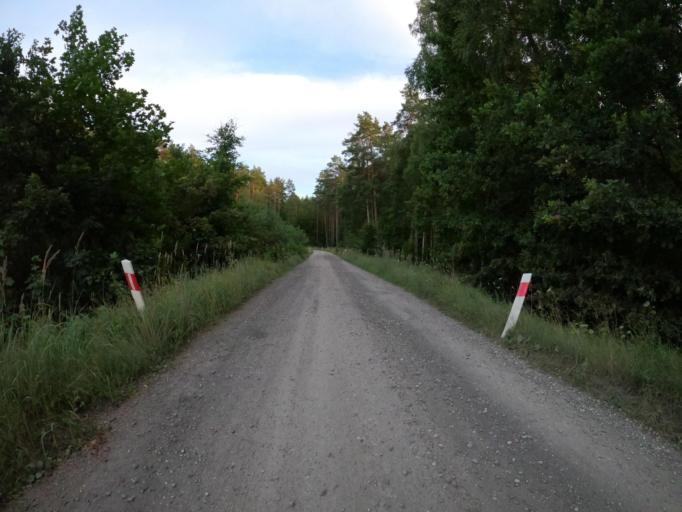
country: PL
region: West Pomeranian Voivodeship
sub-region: Powiat koszalinski
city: Sianow
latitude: 54.1043
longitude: 16.3706
